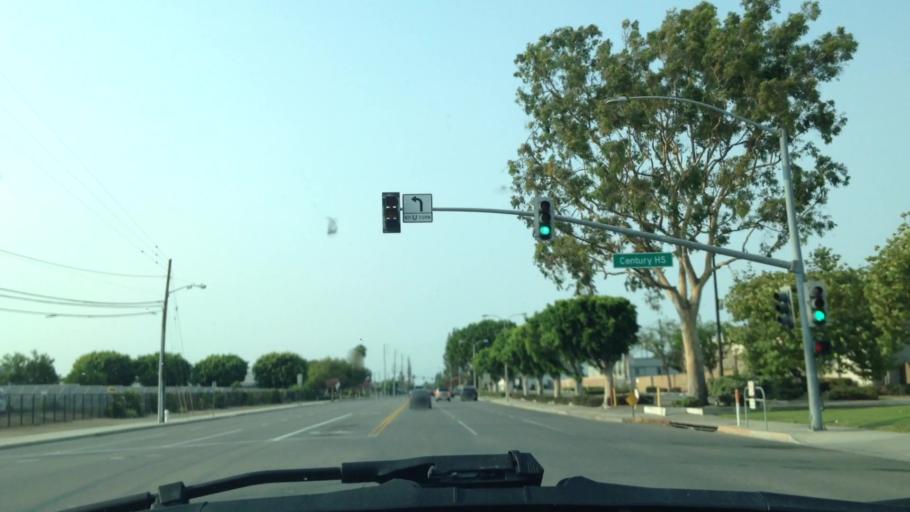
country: US
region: California
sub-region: Orange County
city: Santa Ana
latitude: 33.7301
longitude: -117.8504
